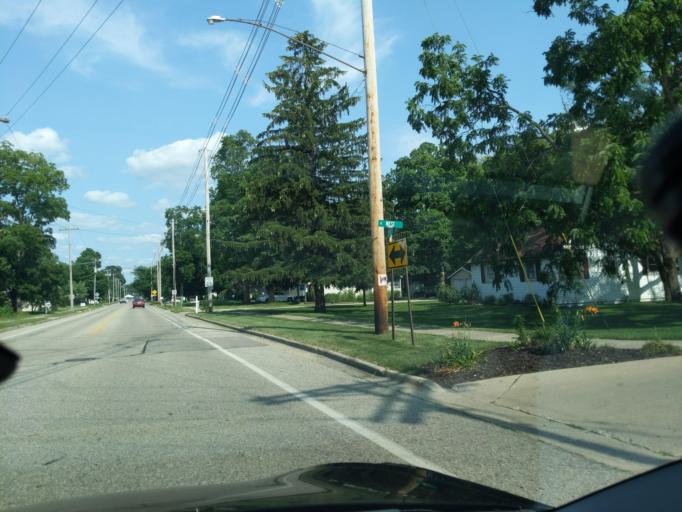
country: US
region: Michigan
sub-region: Kent County
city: Lowell
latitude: 42.9292
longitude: -85.3507
